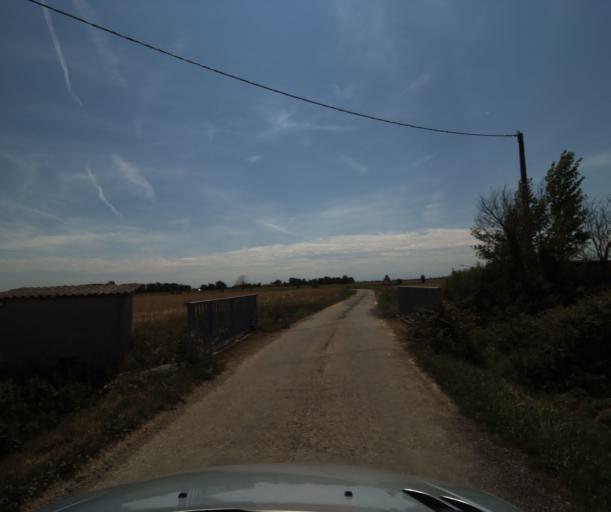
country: FR
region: Midi-Pyrenees
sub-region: Departement de la Haute-Garonne
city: Labastidette
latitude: 43.4627
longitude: 1.2597
